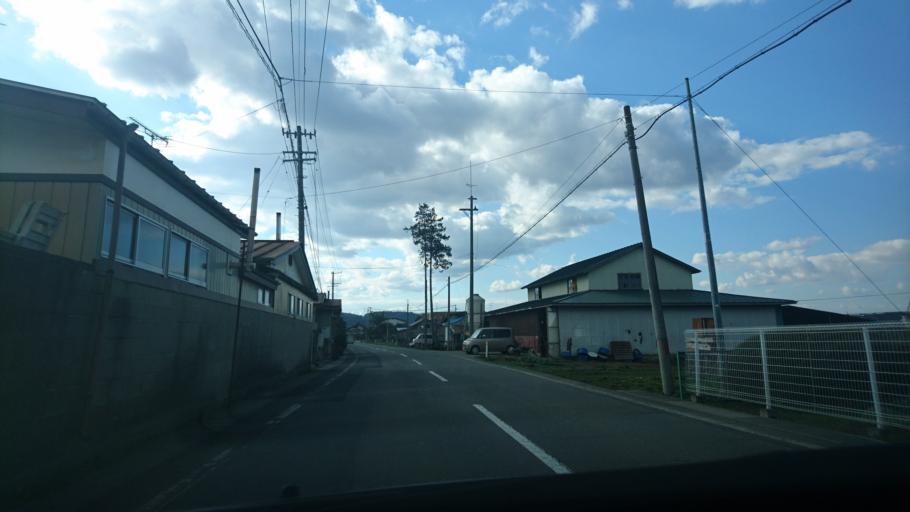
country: JP
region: Iwate
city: Mizusawa
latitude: 39.0433
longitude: 141.1395
